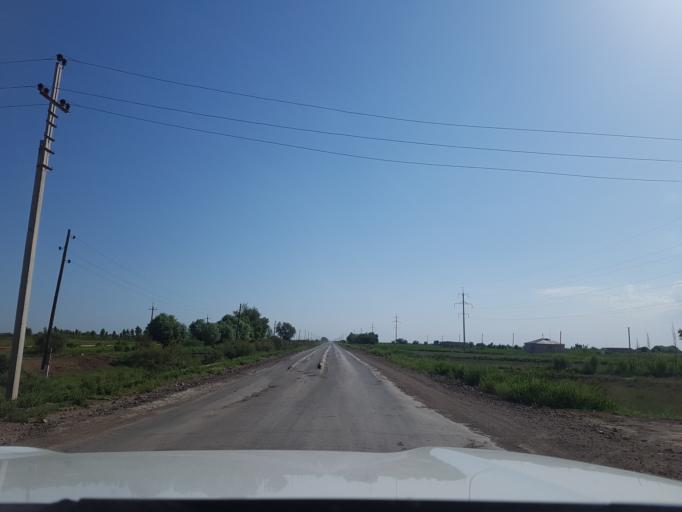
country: TM
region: Dasoguz
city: Koeneuergench
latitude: 42.0984
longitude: 58.8995
